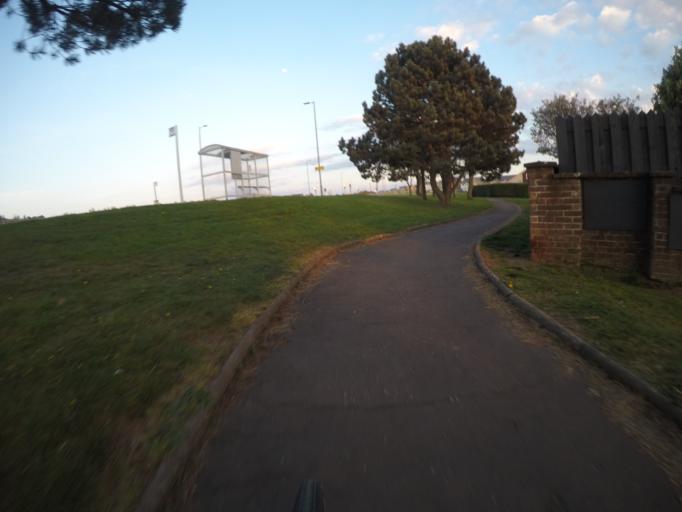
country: GB
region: Scotland
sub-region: South Ayrshire
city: Troon
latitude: 55.5654
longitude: -4.6383
